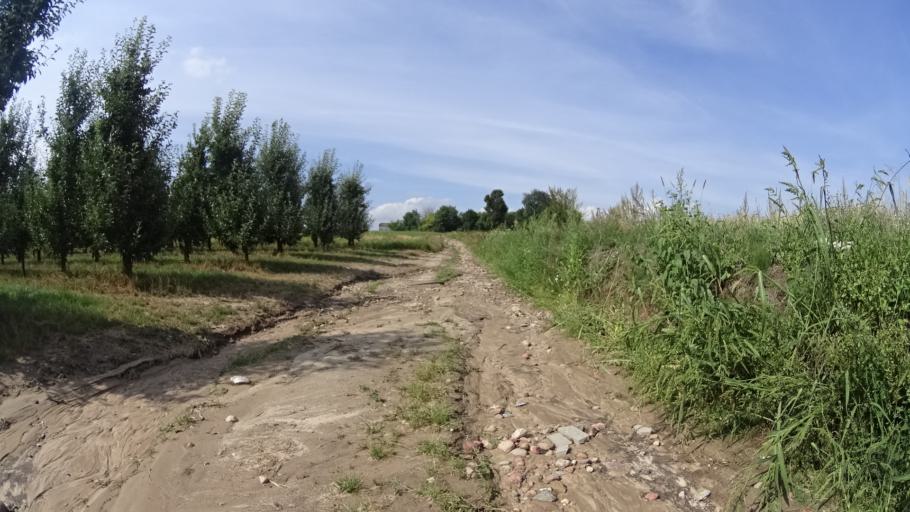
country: PL
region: Masovian Voivodeship
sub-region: Powiat grojecki
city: Goszczyn
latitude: 51.6897
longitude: 20.8393
